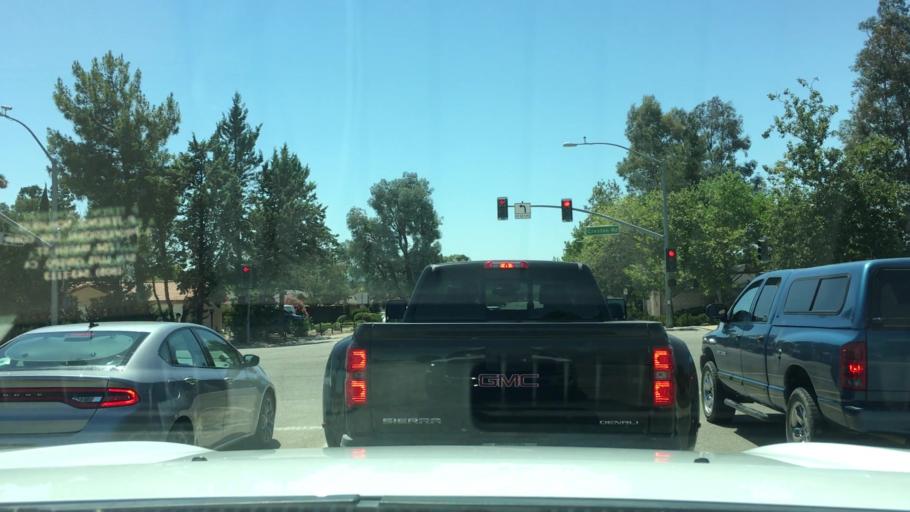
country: US
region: California
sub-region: San Luis Obispo County
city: Paso Robles
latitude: 35.6158
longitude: -120.6588
